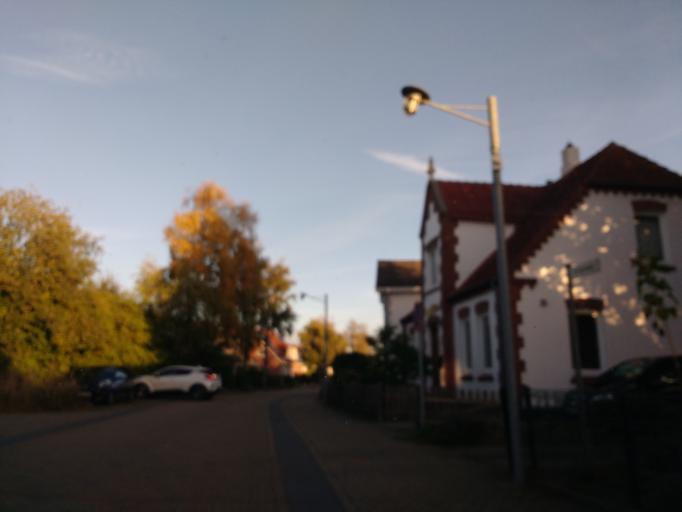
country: DE
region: Schleswig-Holstein
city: Kellenhusen
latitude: 54.1886
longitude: 11.0571
